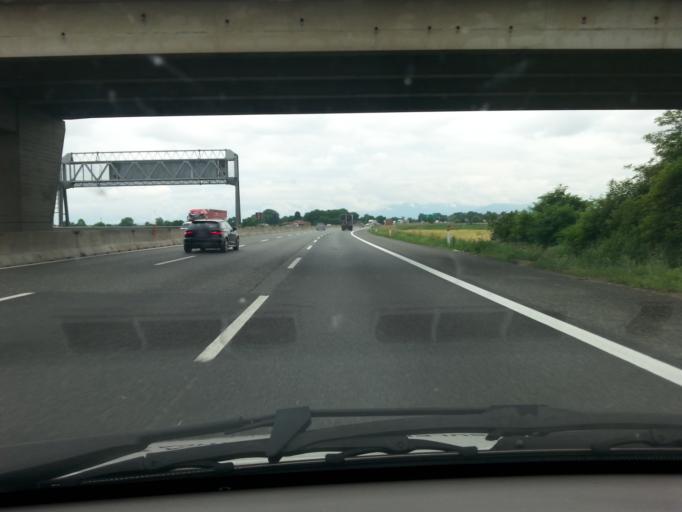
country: IT
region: Piedmont
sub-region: Provincia di Torino
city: Tagliaferro
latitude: 44.9703
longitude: 7.6840
